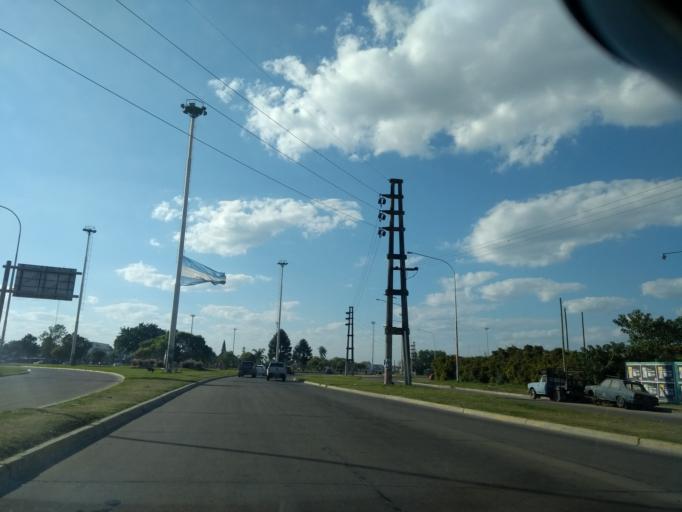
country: AR
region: Corrientes
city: Corrientes
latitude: -27.4842
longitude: -58.7843
